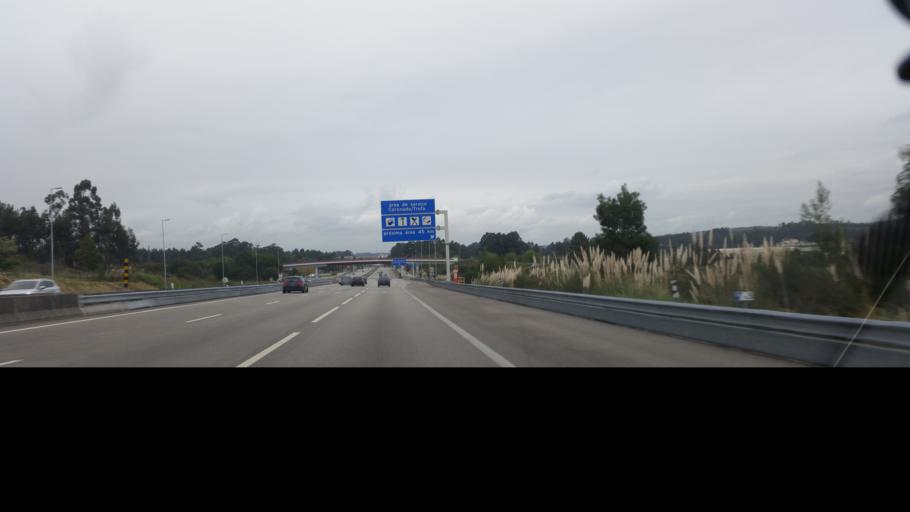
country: PT
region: Porto
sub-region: Trofa
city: Sao Romao do Coronado
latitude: 41.2593
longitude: -8.5662
